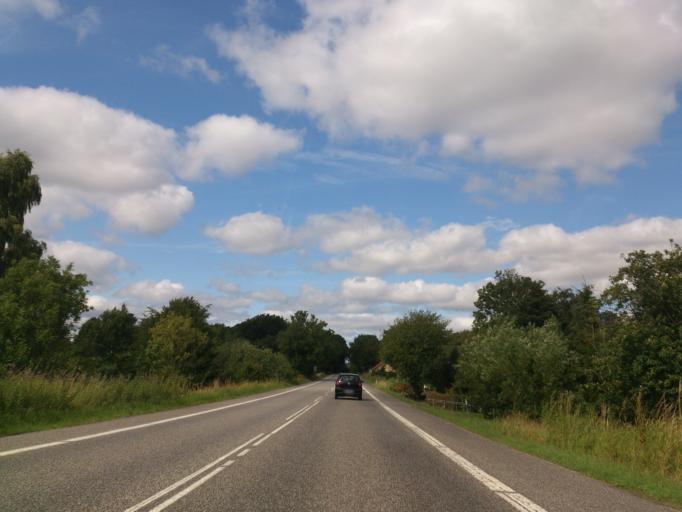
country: DK
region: South Denmark
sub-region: Aabenraa Kommune
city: Krusa
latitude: 54.9315
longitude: 9.4494
